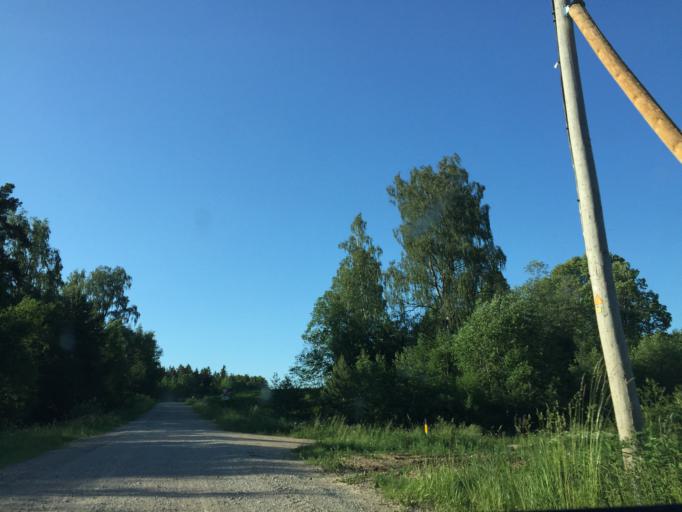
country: LV
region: Kandava
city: Kandava
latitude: 56.8556
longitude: 22.6927
